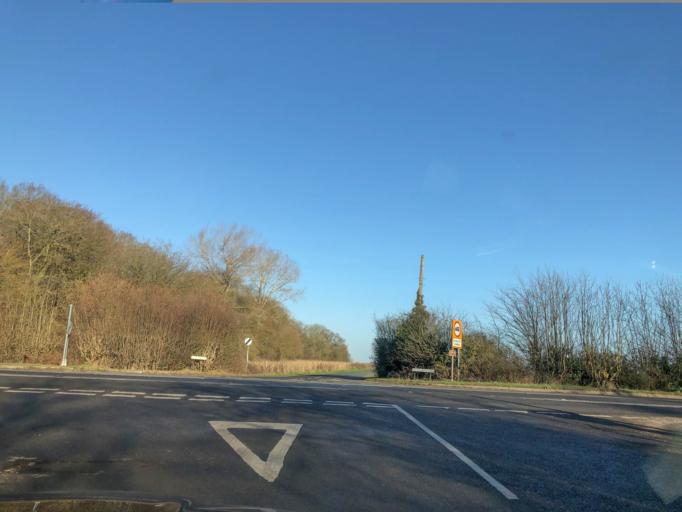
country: GB
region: England
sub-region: Warwickshire
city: Harbury
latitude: 52.2079
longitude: -1.4977
